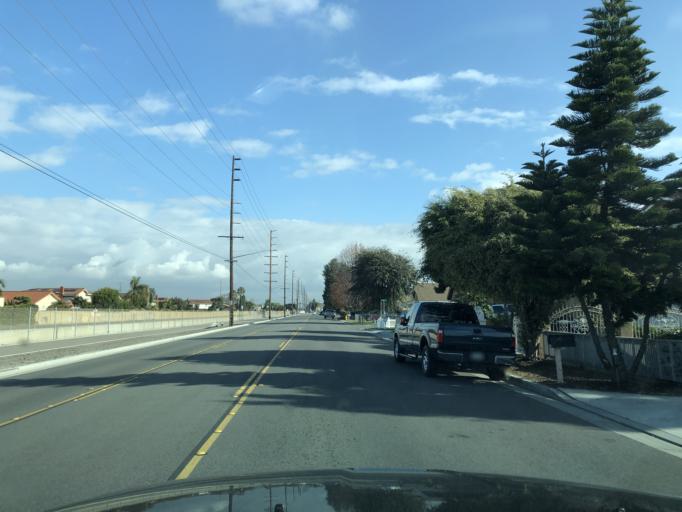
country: US
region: California
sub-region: Orange County
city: Westminster
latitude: 33.7565
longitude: -118.0331
